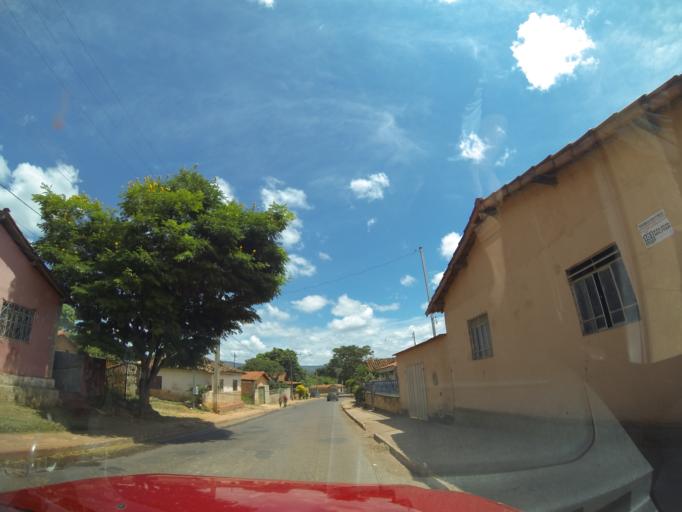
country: BR
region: Minas Gerais
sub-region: Diamantina
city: Diamantina
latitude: -18.0844
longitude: -43.4772
